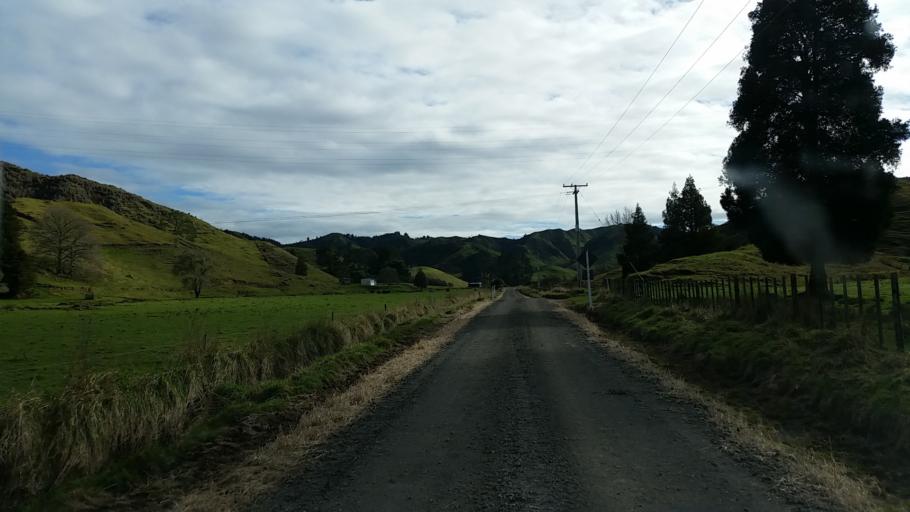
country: NZ
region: Taranaki
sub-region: South Taranaki District
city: Eltham
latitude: -39.2333
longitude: 174.5680
